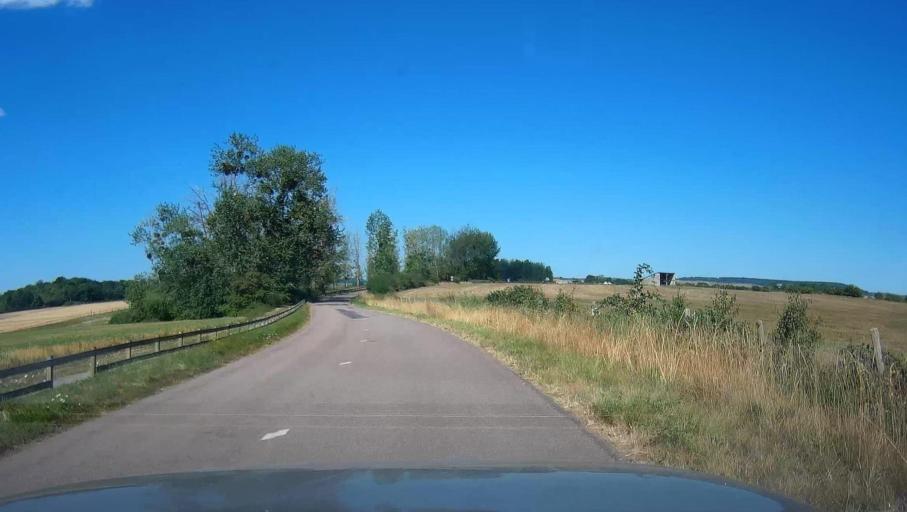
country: FR
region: Champagne-Ardenne
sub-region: Departement de la Haute-Marne
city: Langres
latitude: 47.8763
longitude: 5.3759
